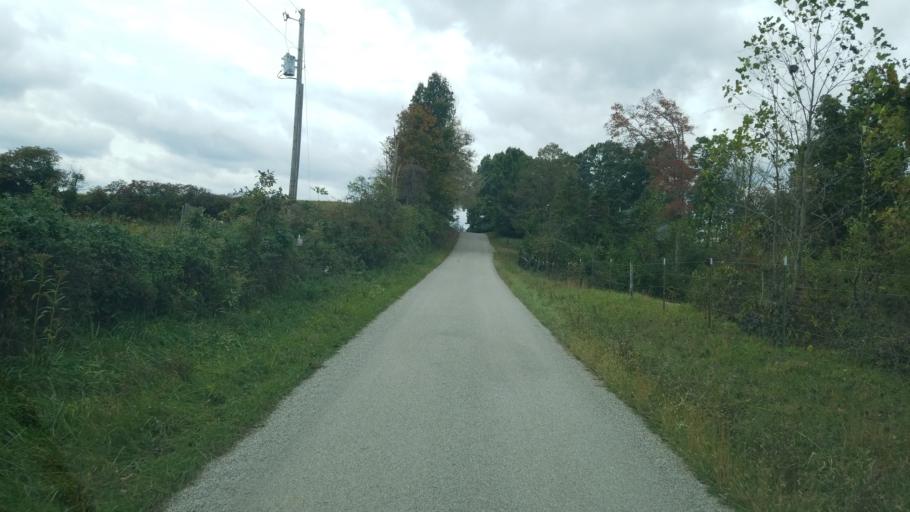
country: US
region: Ohio
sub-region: Jackson County
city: Wellston
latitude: 39.1690
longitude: -82.5554
